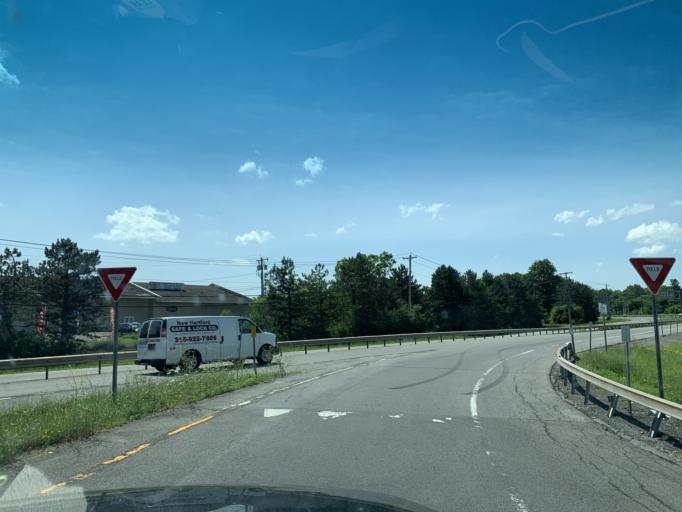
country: US
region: New York
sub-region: Oneida County
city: New Hartford
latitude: 43.0789
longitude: -75.2919
